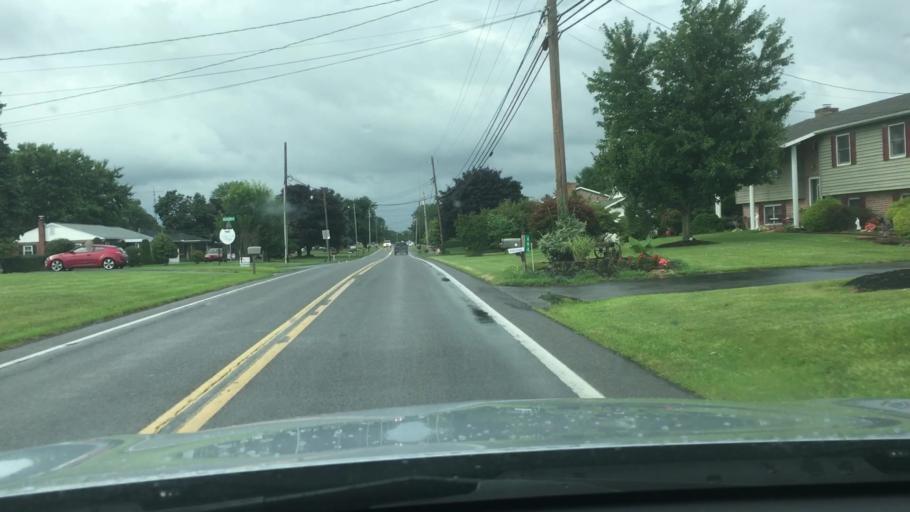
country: US
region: Pennsylvania
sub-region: Franklin County
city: Chambersburg
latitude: 39.9148
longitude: -77.7049
